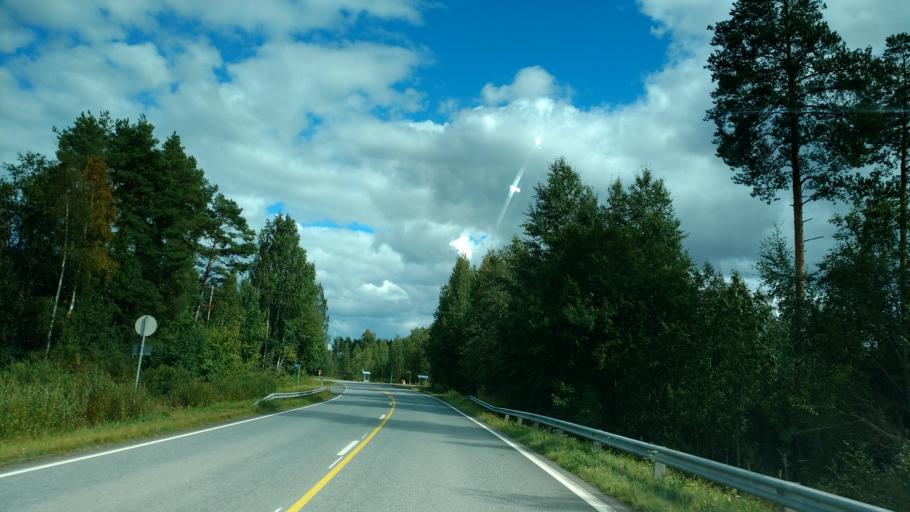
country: FI
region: Haeme
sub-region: Forssa
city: Ypaejae
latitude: 60.7986
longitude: 23.2098
